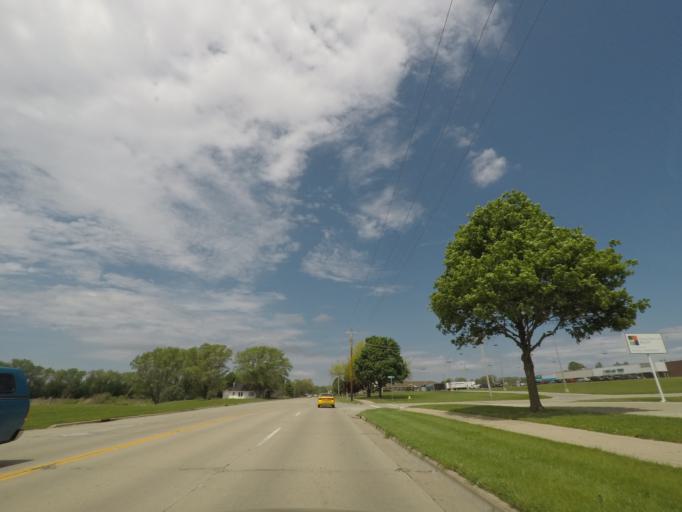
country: US
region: Wisconsin
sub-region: Rock County
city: Beloit
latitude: 42.5202
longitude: -89.0678
